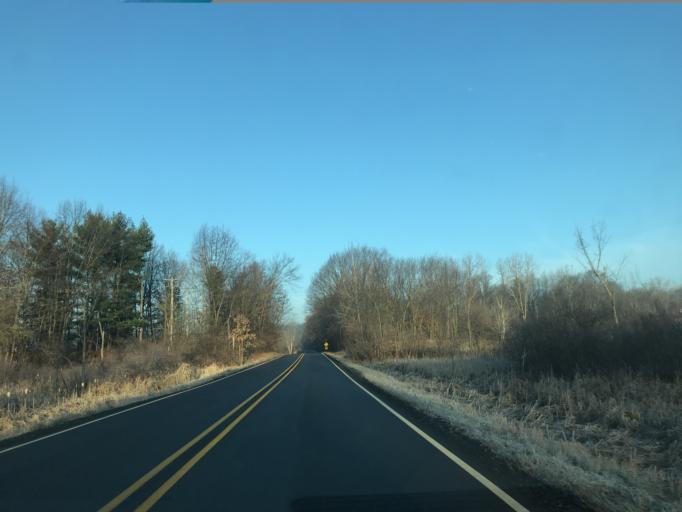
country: US
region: Michigan
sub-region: Ingham County
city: Leslie
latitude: 42.4327
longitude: -84.5347
